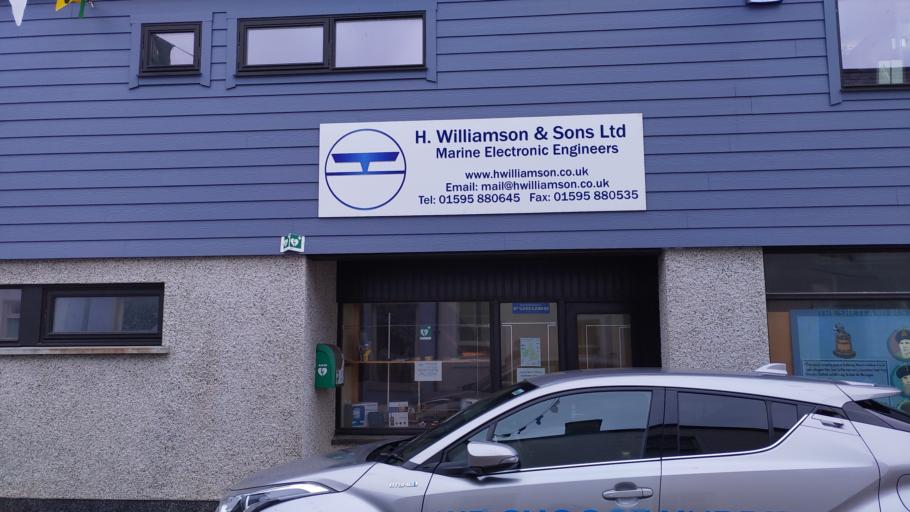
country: GB
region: Scotland
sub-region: Shetland Islands
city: Lerwick
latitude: 60.1371
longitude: -1.2759
